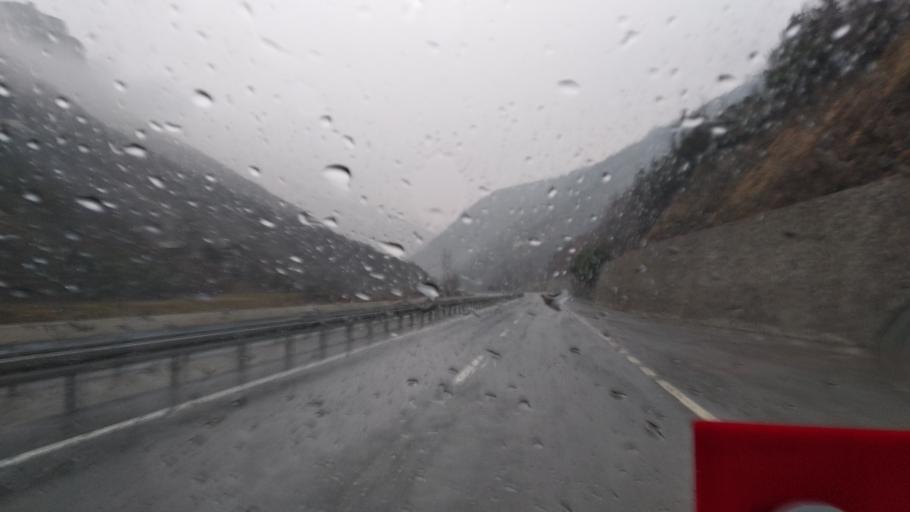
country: TR
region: Trabzon
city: Macka
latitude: 40.7837
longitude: 39.5746
